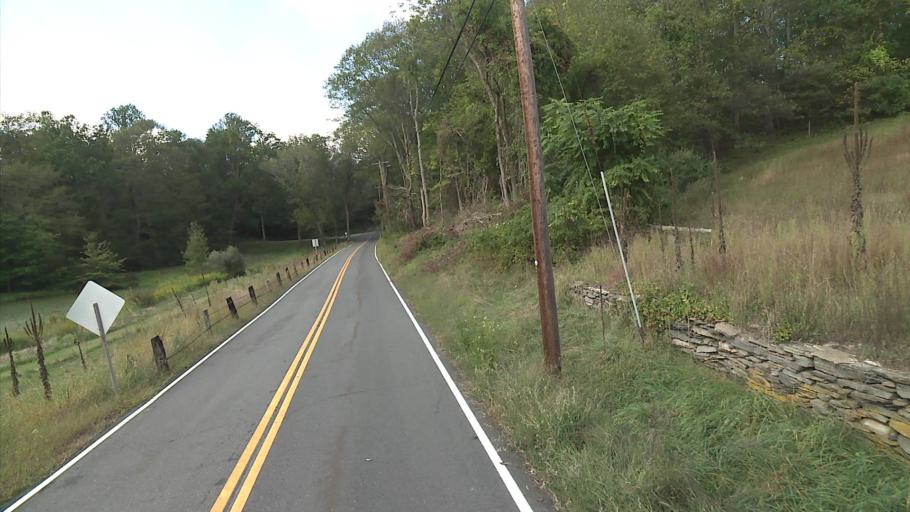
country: US
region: Connecticut
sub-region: Middlesex County
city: Chester Center
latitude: 41.4295
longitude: -72.4255
